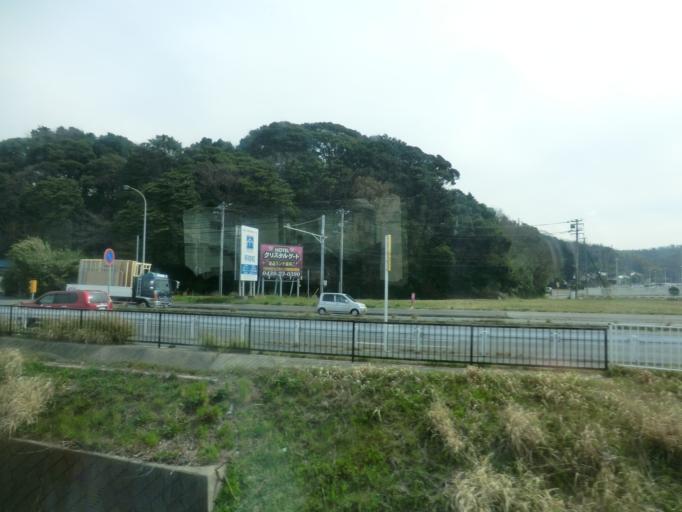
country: JP
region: Chiba
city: Kisarazu
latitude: 35.3631
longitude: 139.9223
